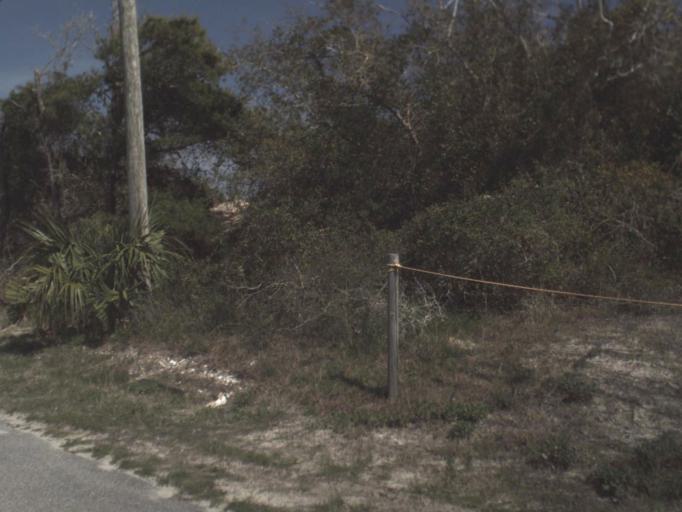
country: US
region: Florida
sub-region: Franklin County
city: Carrabelle
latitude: 29.8002
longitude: -84.7421
